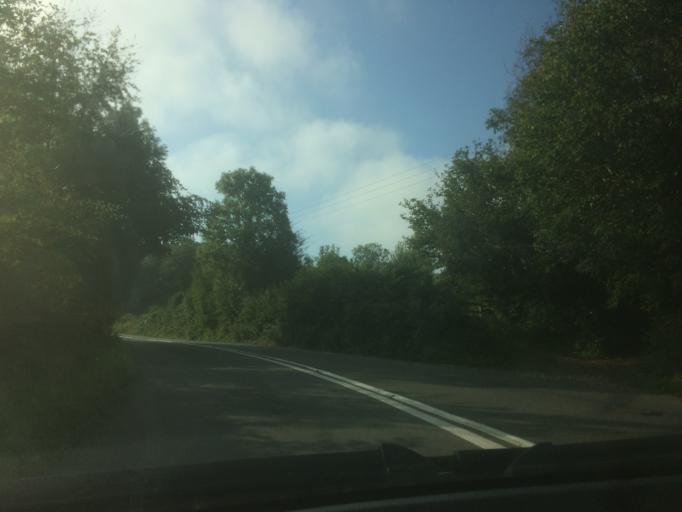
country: GB
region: England
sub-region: Devon
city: Tavistock
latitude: 50.5363
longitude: -4.1768
